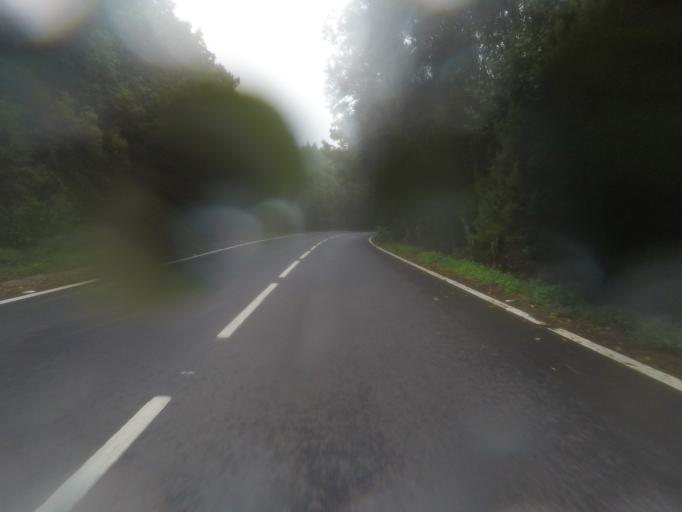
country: ES
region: Canary Islands
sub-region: Provincia de Santa Cruz de Tenerife
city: Vallehermosa
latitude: 28.1365
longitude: -17.2815
